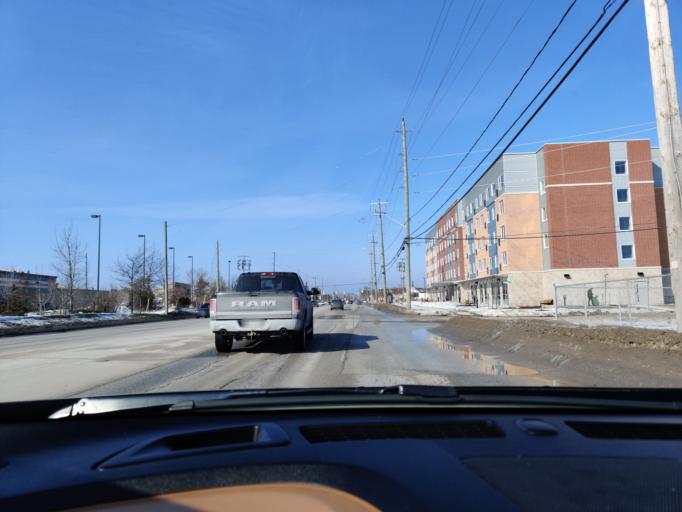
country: CA
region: Ontario
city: Collingwood
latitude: 44.4988
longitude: -80.2339
